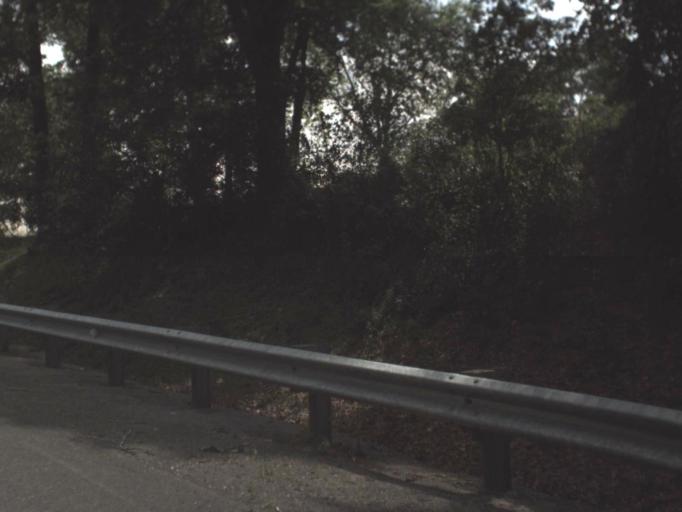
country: US
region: Alabama
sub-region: Escambia County
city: East Brewton
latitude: 30.9964
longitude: -87.1154
